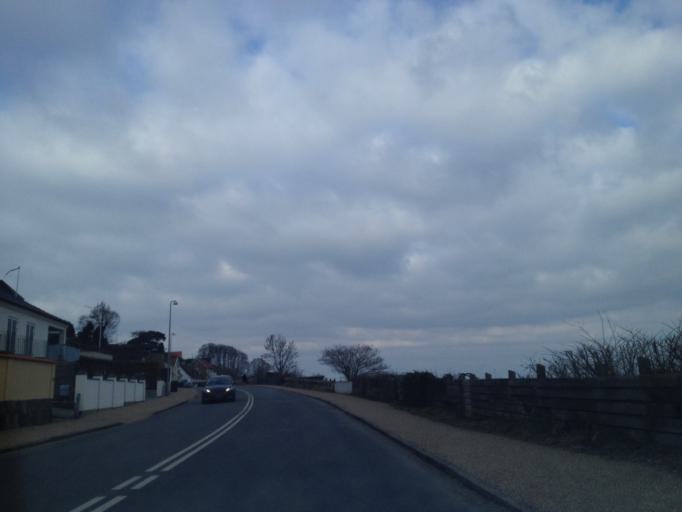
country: DK
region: Capital Region
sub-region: Helsingor Kommune
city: Helsingor
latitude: 56.0178
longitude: 12.6009
